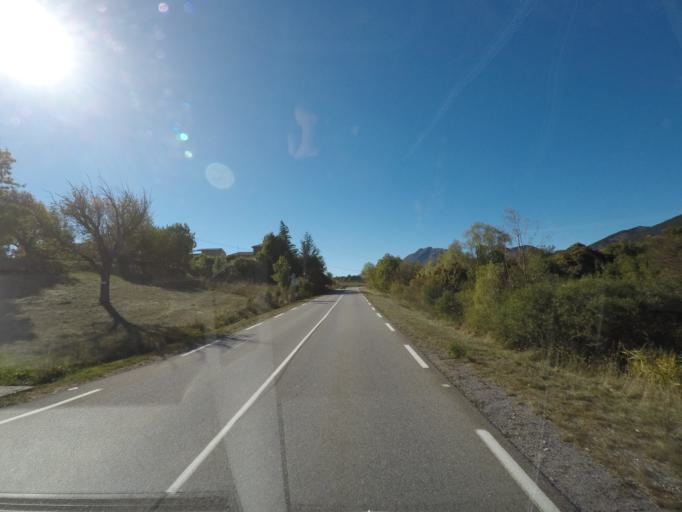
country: FR
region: Provence-Alpes-Cote d'Azur
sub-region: Departement des Hautes-Alpes
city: Serres
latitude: 44.4157
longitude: 5.6082
